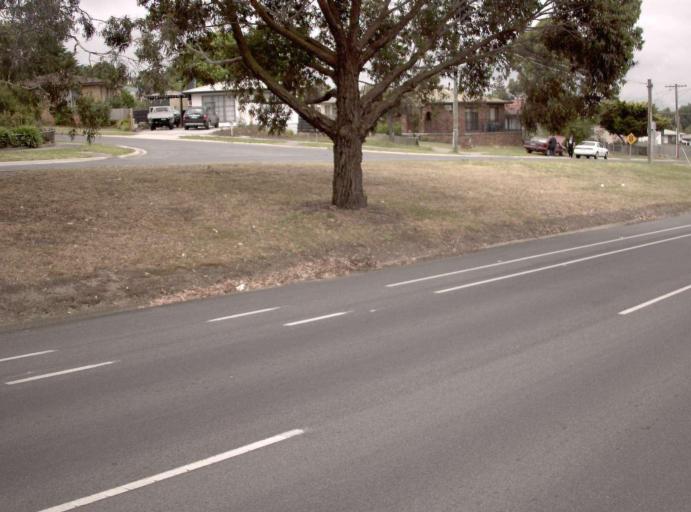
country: AU
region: Victoria
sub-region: Latrobe
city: Morwell
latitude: -38.2401
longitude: 146.4189
